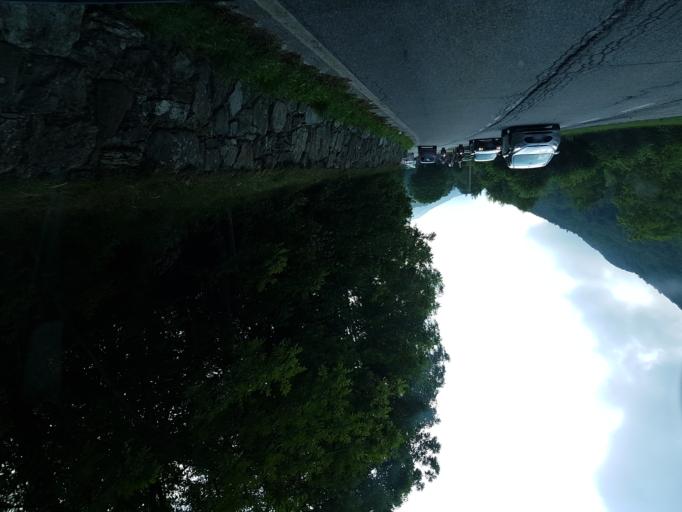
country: IT
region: Piedmont
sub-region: Provincia di Cuneo
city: Sampeyre
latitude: 44.5792
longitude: 7.1582
